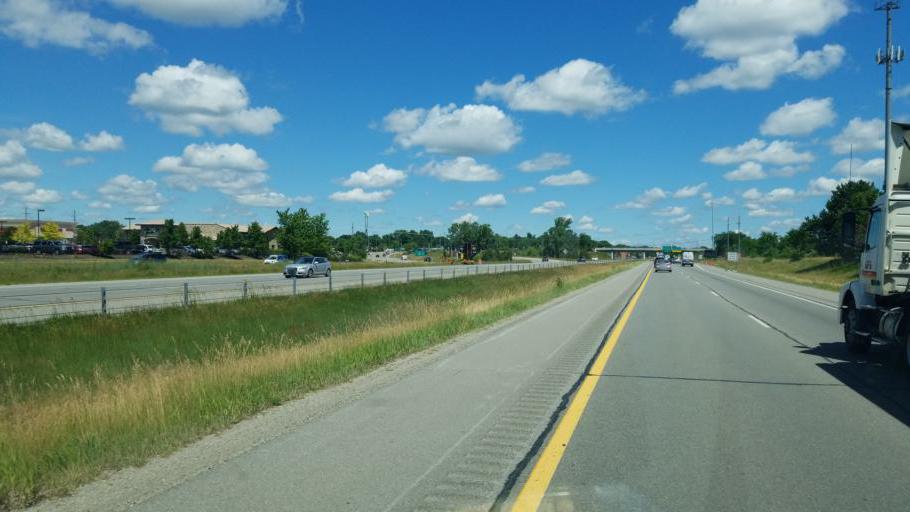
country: US
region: Michigan
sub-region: Livingston County
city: Brighton
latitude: 42.5016
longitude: -83.7577
